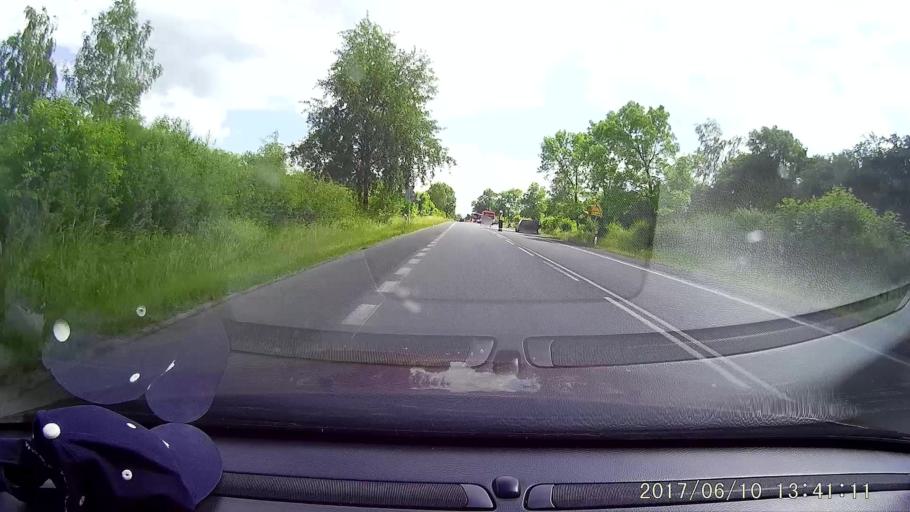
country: PL
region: Lower Silesian Voivodeship
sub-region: Powiat zgorzelecki
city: Zgorzelec
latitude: 51.1041
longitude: 15.0179
